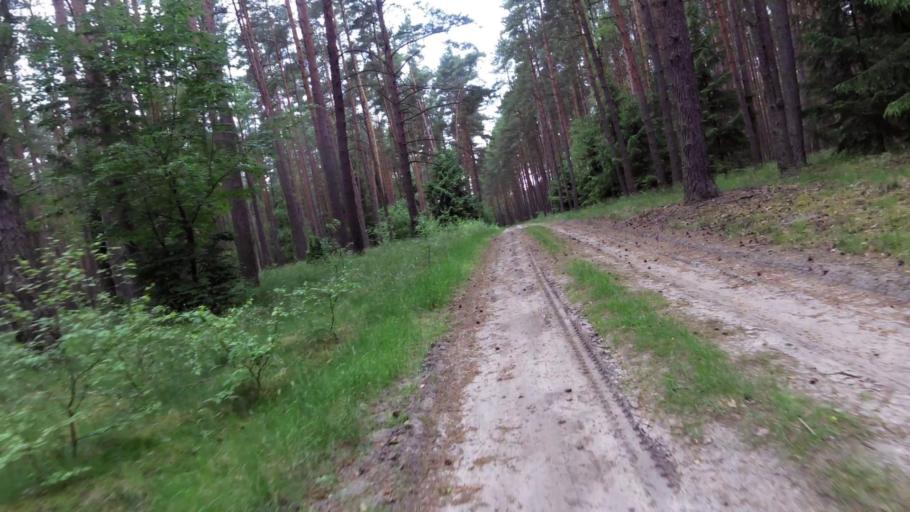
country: PL
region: West Pomeranian Voivodeship
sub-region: Powiat mysliborski
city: Debno
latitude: 52.8194
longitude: 14.6513
